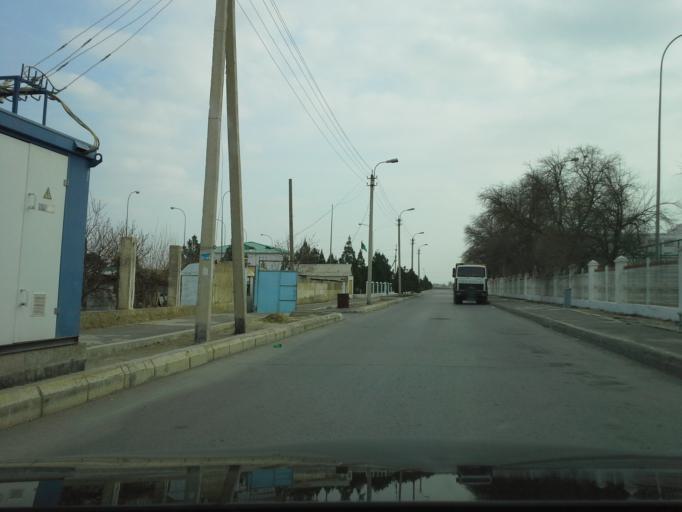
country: TM
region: Ahal
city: Abadan
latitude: 38.0371
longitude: 58.2677
